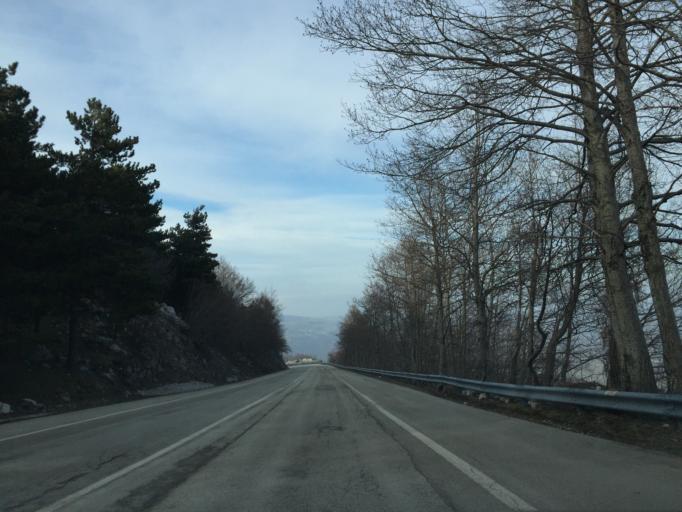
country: IT
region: Molise
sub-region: Provincia di Campobasso
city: San Massimo
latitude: 41.4719
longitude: 14.4144
